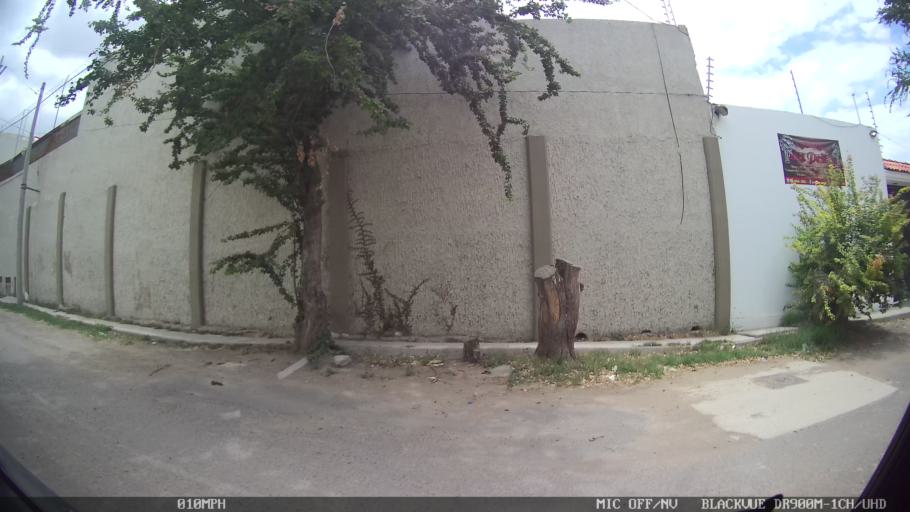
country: MX
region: Jalisco
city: Tlaquepaque
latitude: 20.6385
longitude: -103.2711
